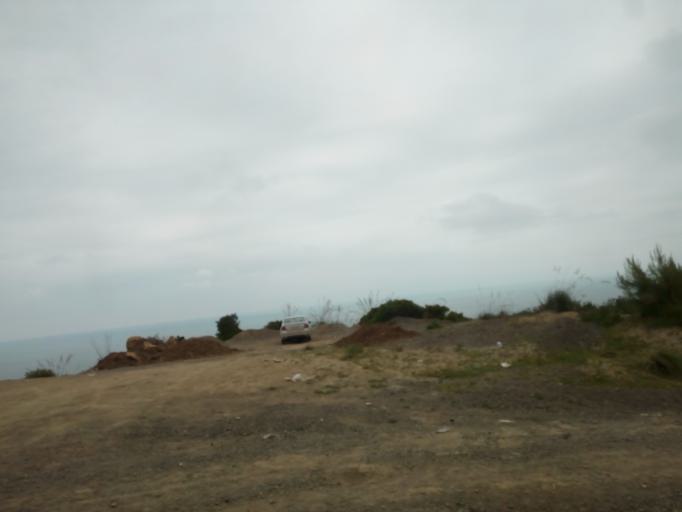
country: DZ
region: Tipaza
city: Tipasa
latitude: 36.5853
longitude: 2.5453
